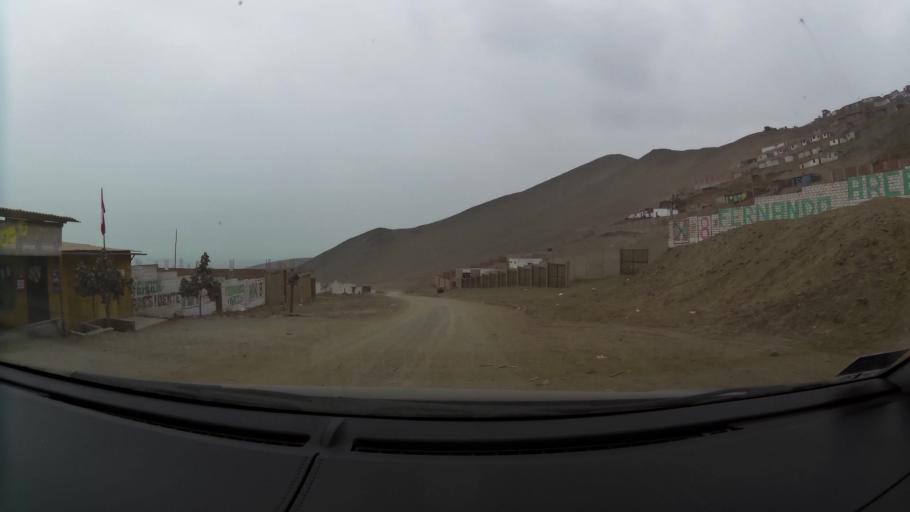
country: PE
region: Lima
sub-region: Lima
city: Santa Rosa
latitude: -11.8147
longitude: -77.1694
